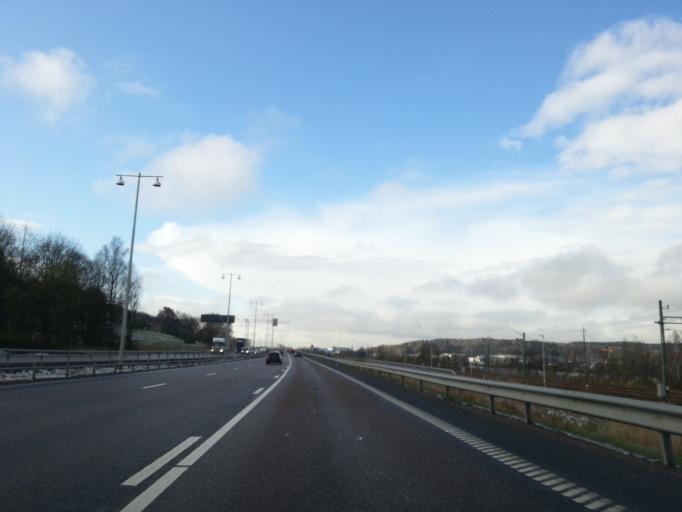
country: SE
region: Vaestra Goetaland
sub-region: Goteborg
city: Hammarkullen
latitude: 57.7850
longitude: 12.0096
